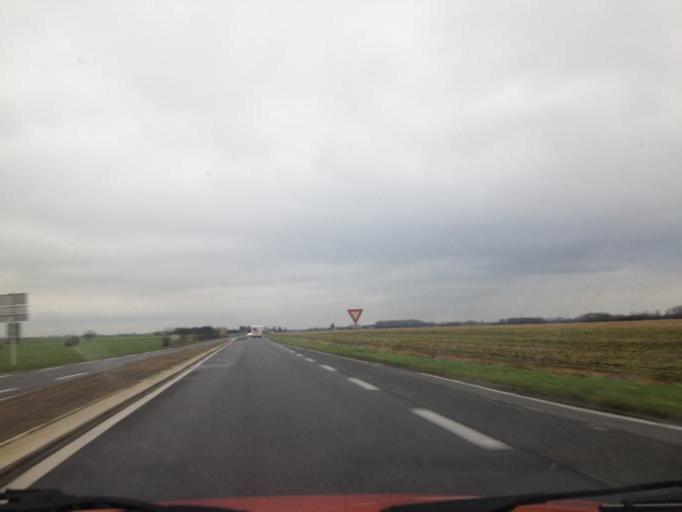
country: FR
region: Auvergne
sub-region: Departement de l'Allier
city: Bessay-sur-Allier
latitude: 46.3874
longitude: 3.3583
